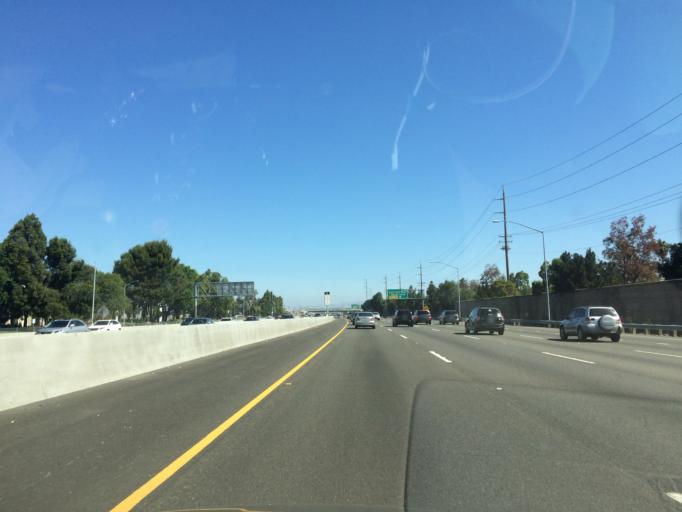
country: US
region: California
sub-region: Santa Clara County
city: Milpitas
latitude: 37.4073
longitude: -121.9103
